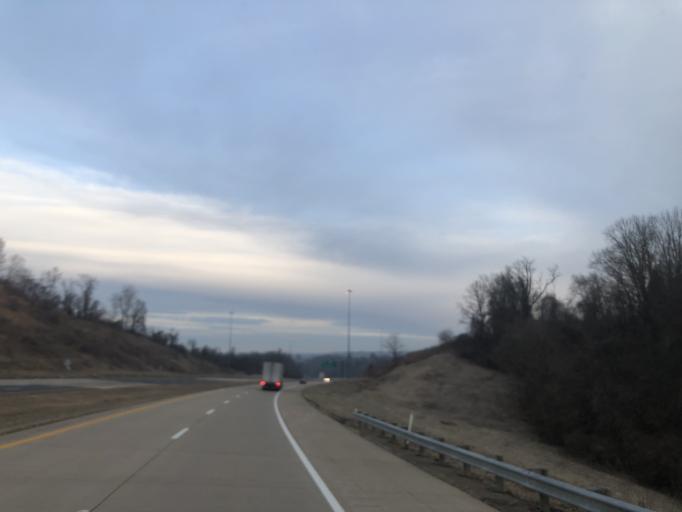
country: US
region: Ohio
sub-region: Athens County
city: Athens
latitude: 39.2932
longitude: -82.1032
